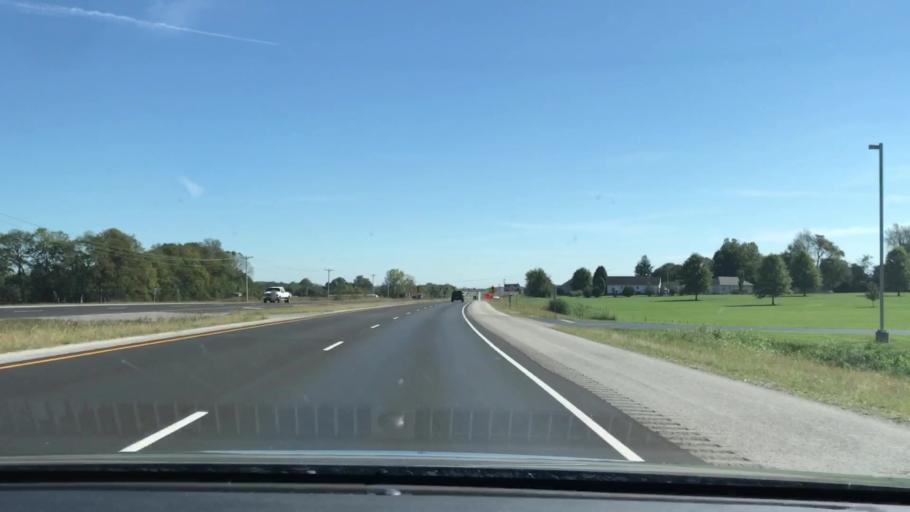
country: US
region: Kentucky
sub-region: Logan County
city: Auburn
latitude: 36.8703
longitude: -86.7207
